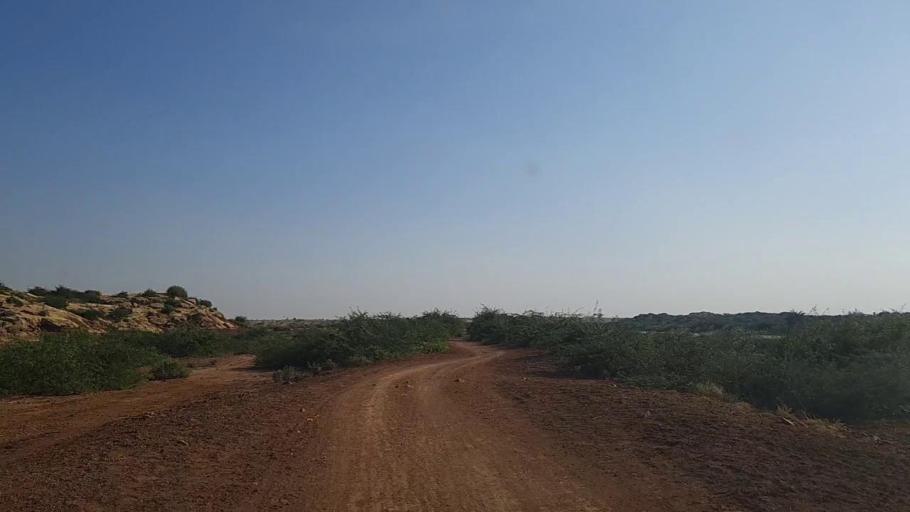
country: PK
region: Sindh
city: Daro Mehar
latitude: 25.0323
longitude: 68.1391
